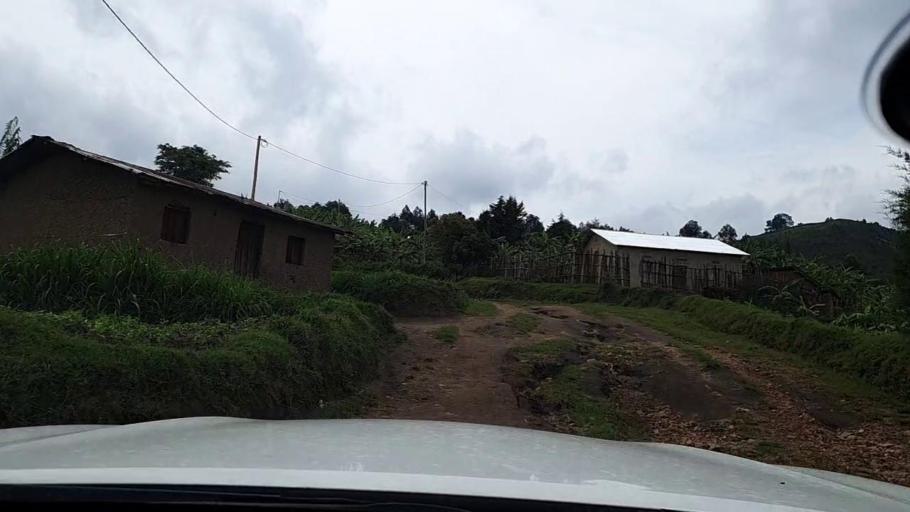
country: RW
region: Western Province
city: Kibuye
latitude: -2.1978
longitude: 29.3191
